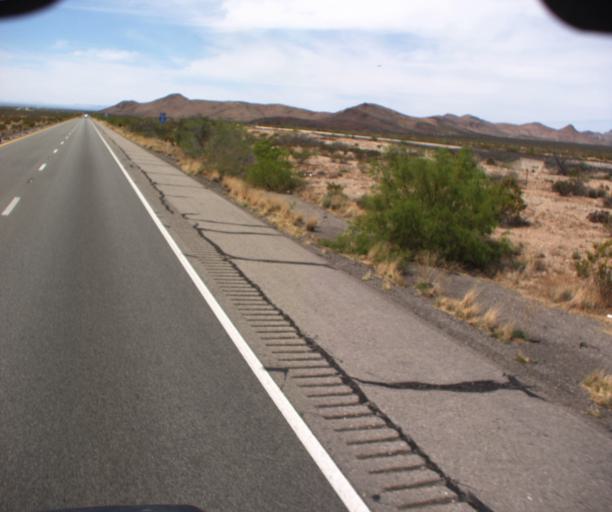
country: US
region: New Mexico
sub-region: Hidalgo County
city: Lordsburg
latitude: 32.2317
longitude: -109.0625
